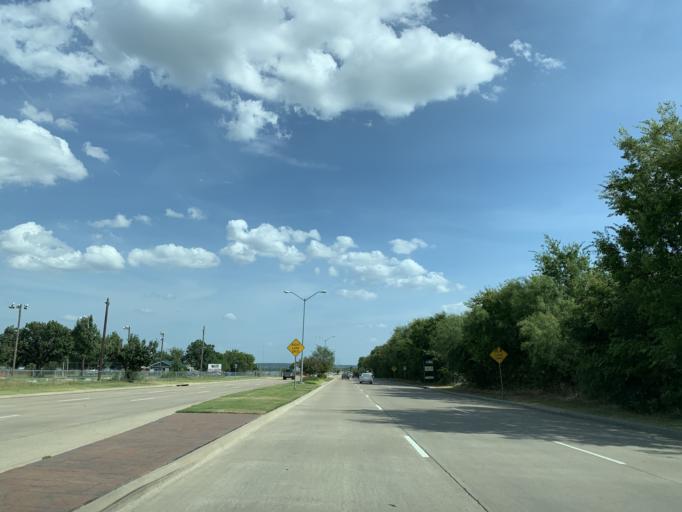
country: US
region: Texas
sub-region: Dallas County
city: Cedar Hill
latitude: 32.6342
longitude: -97.0442
